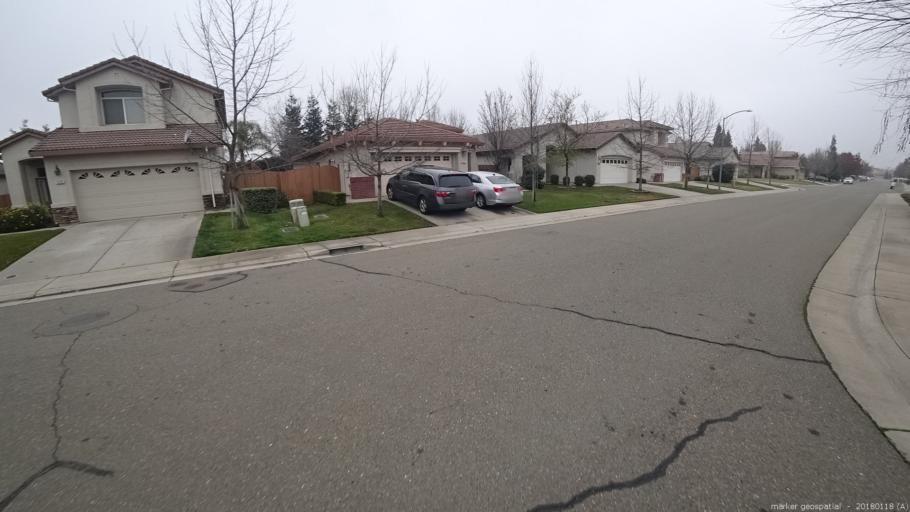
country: US
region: California
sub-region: Sacramento County
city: Rancho Cordova
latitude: 38.5731
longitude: -121.2881
